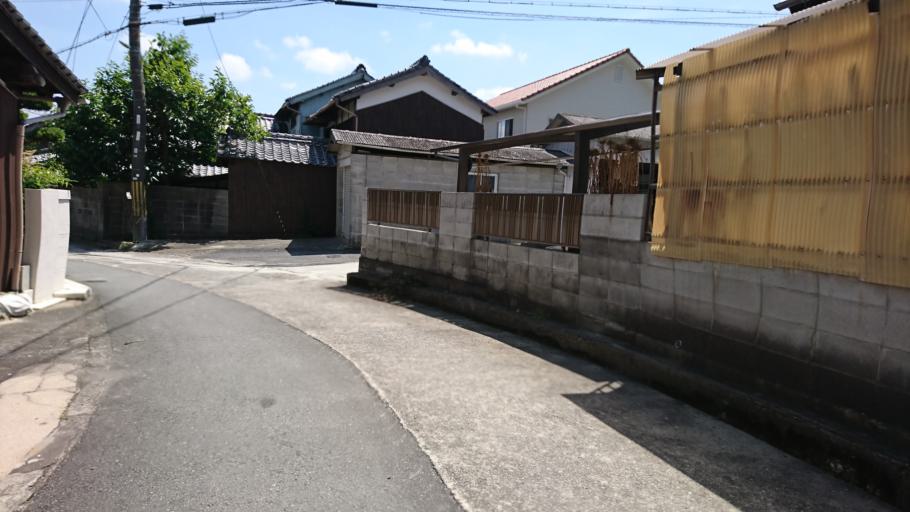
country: JP
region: Hyogo
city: Kakogawacho-honmachi
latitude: 34.8074
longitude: 134.7900
